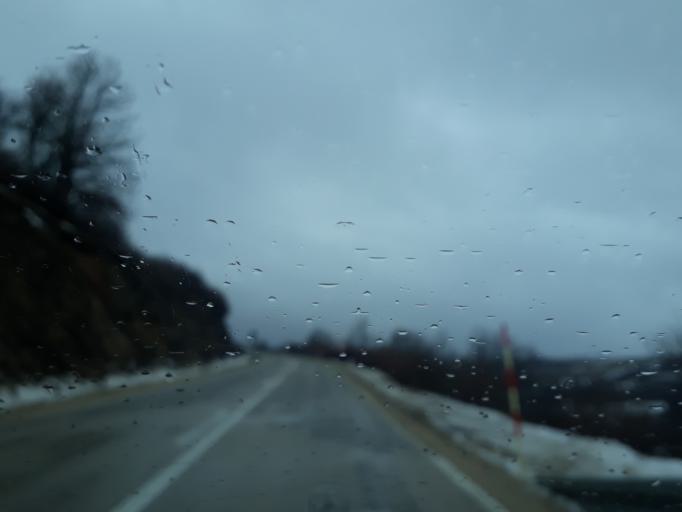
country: BA
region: Federation of Bosnia and Herzegovina
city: Tomislavgrad
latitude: 43.8030
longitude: 17.2049
